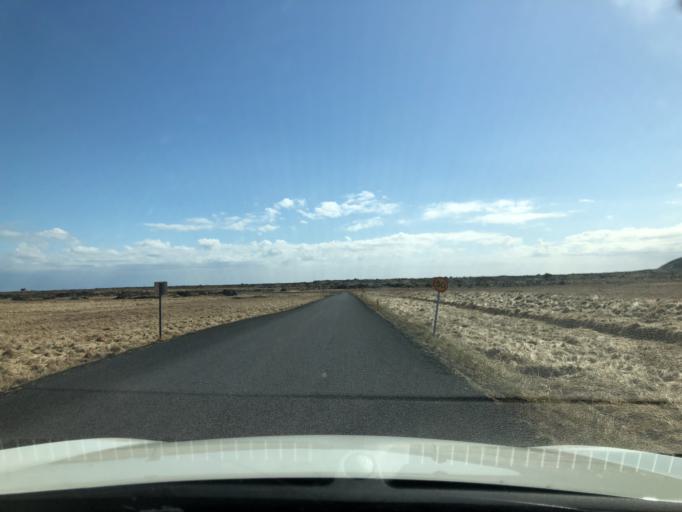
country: IS
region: West
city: Olafsvik
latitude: 64.8318
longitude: -23.4064
